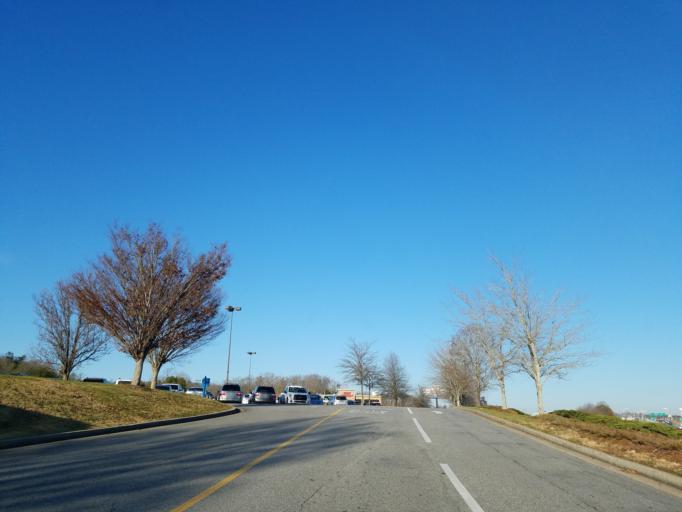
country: US
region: Georgia
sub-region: Dawson County
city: Dawsonville
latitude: 34.3574
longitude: -84.0459
